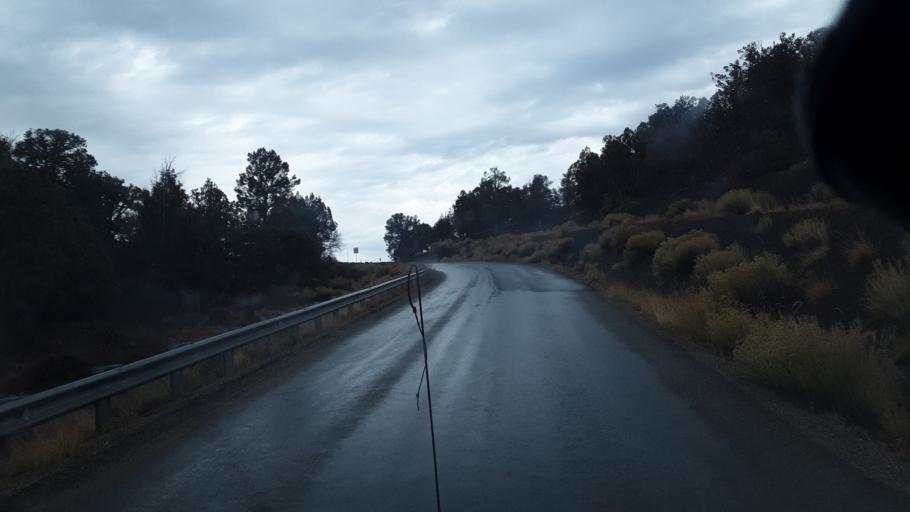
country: US
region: Colorado
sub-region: La Plata County
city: Durango
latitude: 37.2393
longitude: -107.9049
